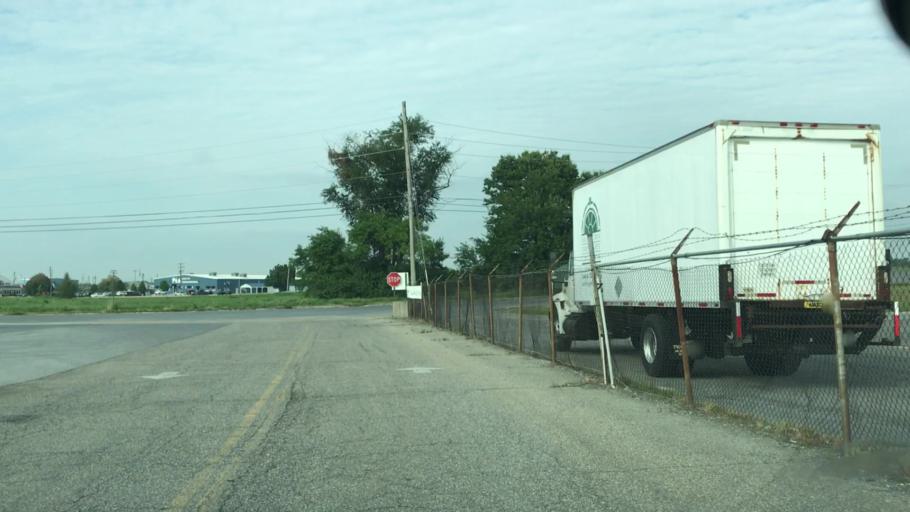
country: US
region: Pennsylvania
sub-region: Franklin County
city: State Line
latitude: 39.7162
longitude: -77.7217
